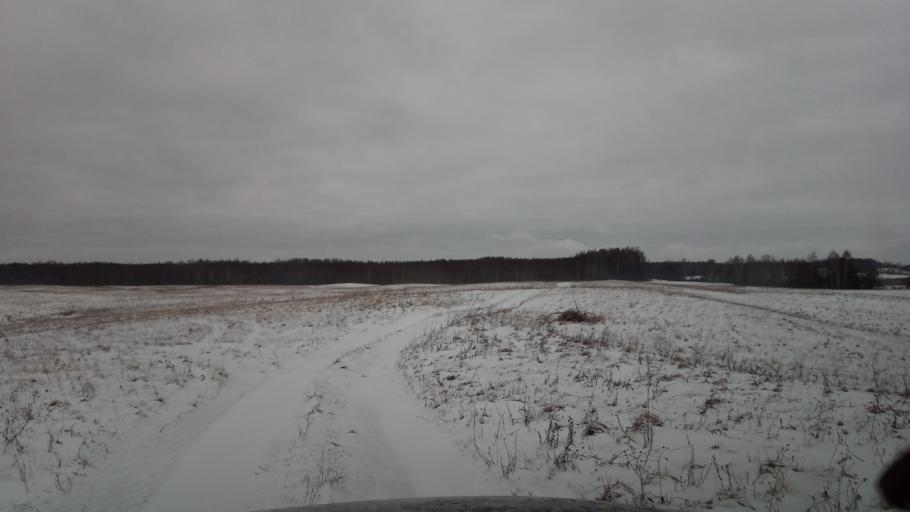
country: LT
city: Zarasai
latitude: 55.6882
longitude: 26.0922
